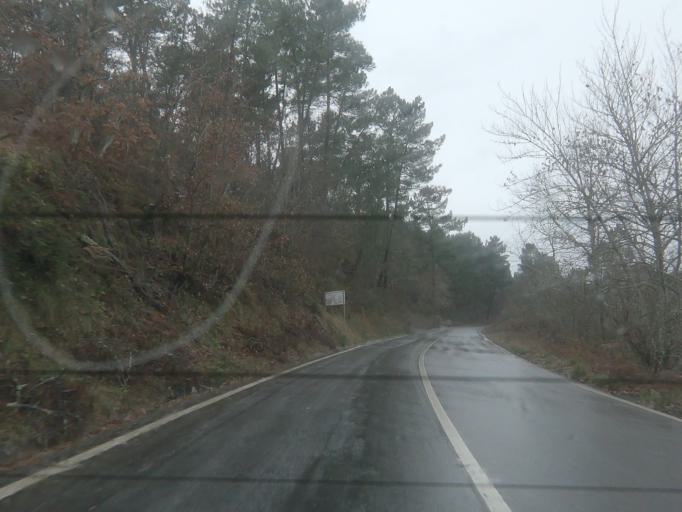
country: PT
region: Vila Real
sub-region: Vila Real
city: Vila Real
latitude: 41.2554
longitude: -7.6842
